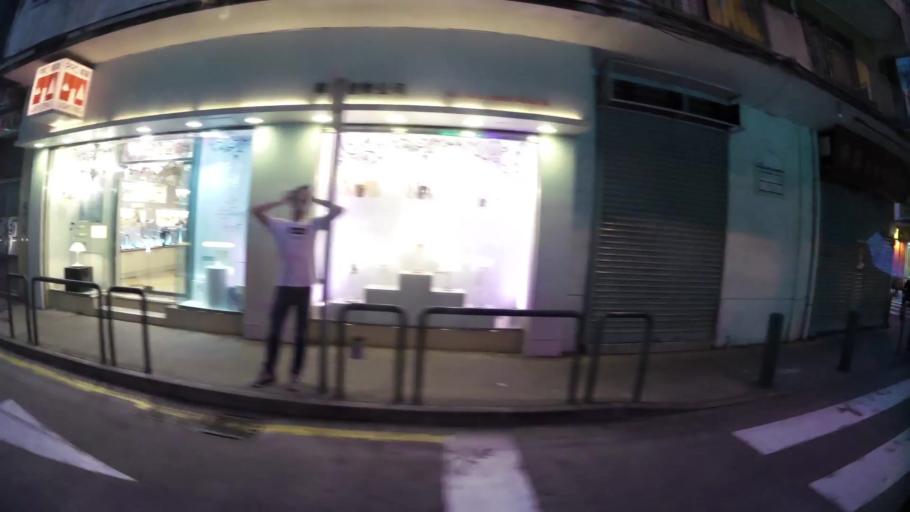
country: MO
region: Macau
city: Macau
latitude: 22.2049
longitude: 113.5467
